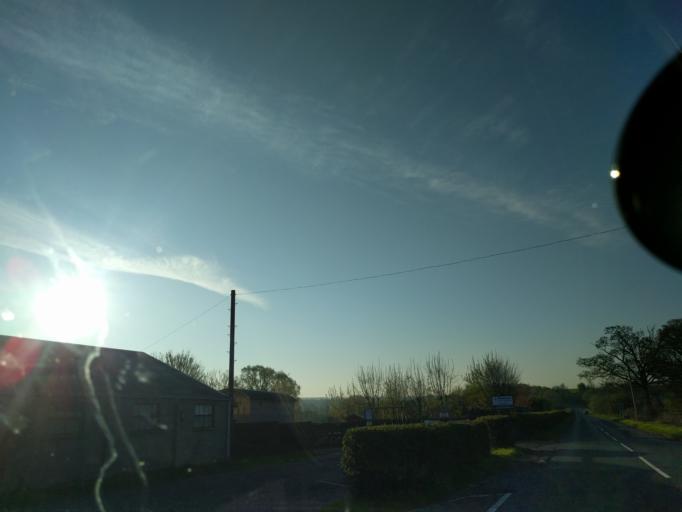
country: GB
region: England
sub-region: Wiltshire
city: Worton
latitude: 51.3097
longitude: -2.0237
